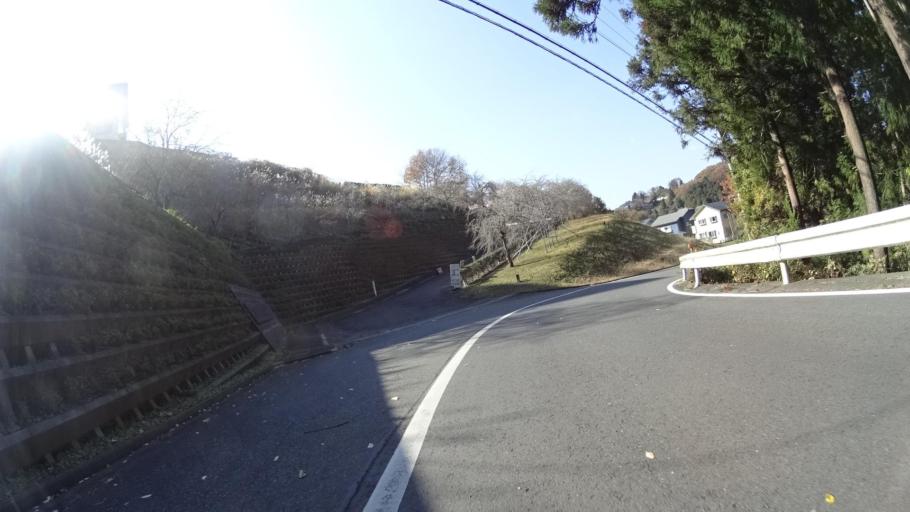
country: JP
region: Yamanashi
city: Uenohara
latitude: 35.5851
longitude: 139.1582
